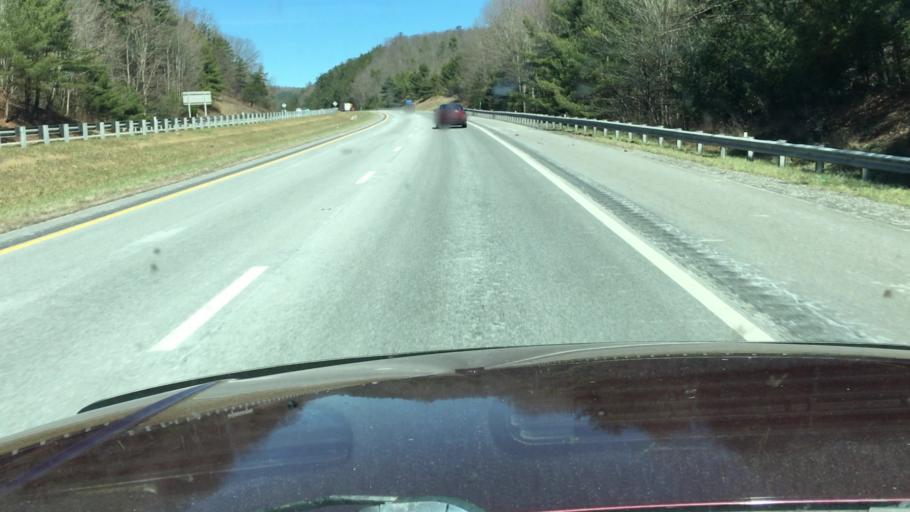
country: US
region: Virginia
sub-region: Bland County
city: Bland
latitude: 37.1270
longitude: -81.1203
